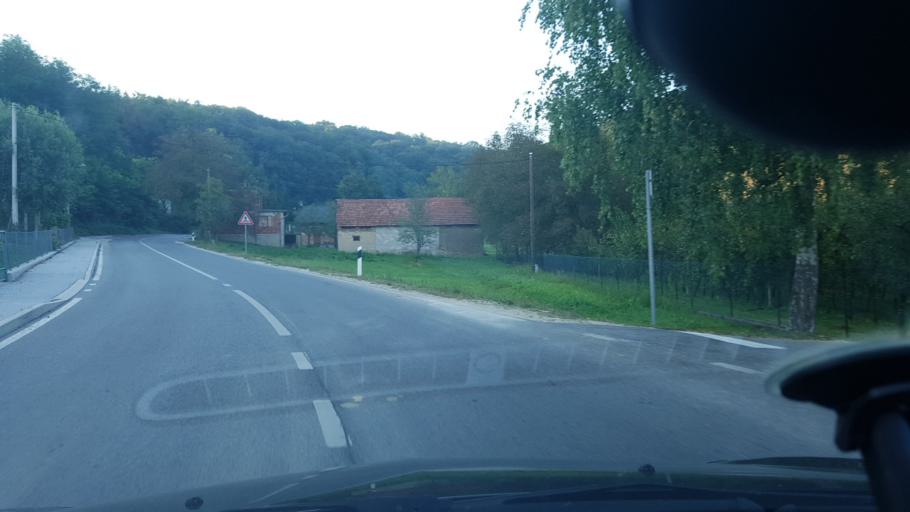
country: HR
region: Krapinsko-Zagorska
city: Pregrada
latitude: 46.1504
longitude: 15.7934
